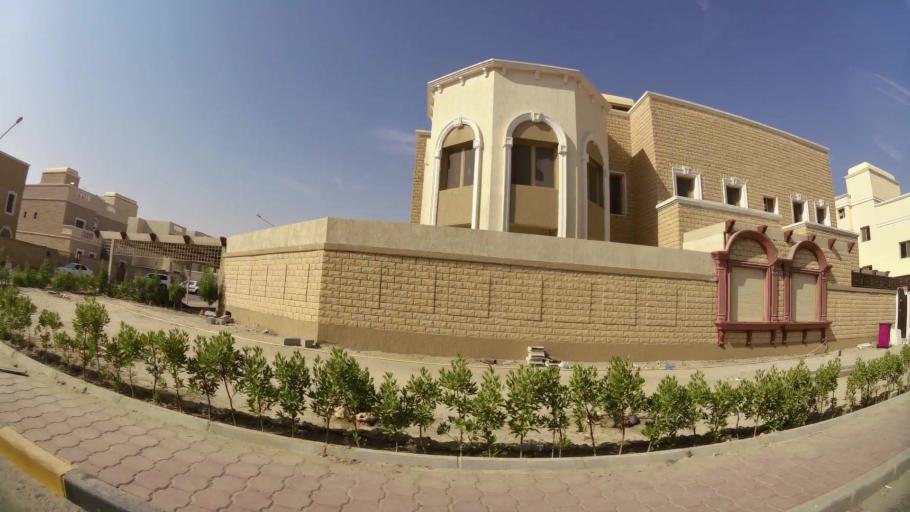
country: KW
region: Al Ahmadi
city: Al Wafrah
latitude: 28.7901
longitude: 48.0689
